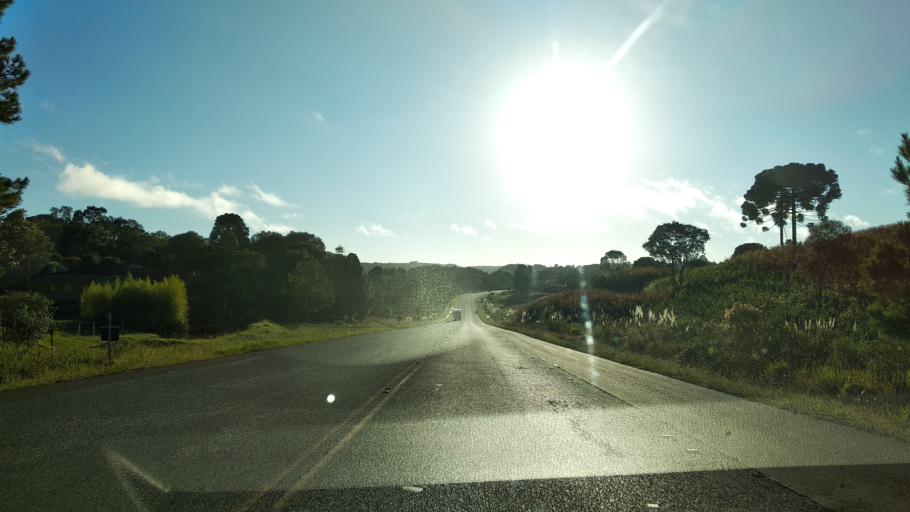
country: BR
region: Santa Catarina
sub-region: Correia Pinto
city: Correia Pinto
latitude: -27.6241
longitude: -50.6506
